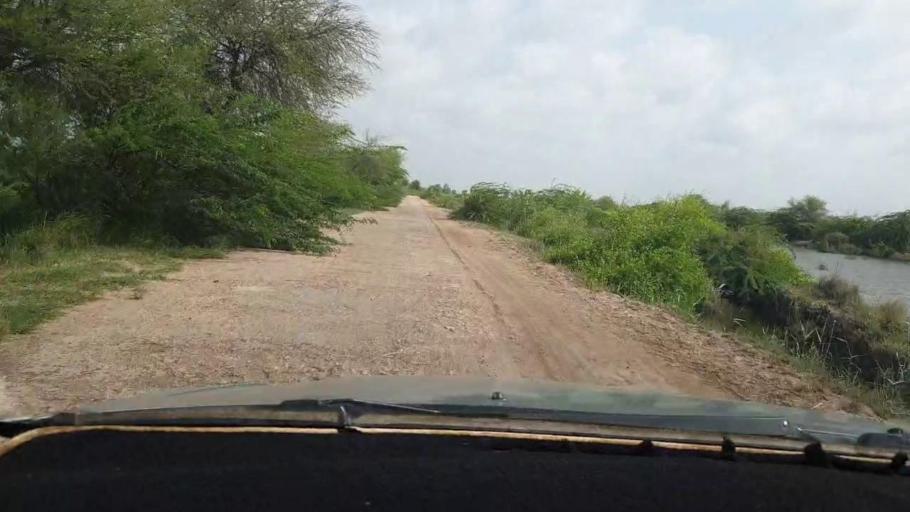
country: PK
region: Sindh
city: Tando Bago
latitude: 24.7799
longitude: 69.0266
